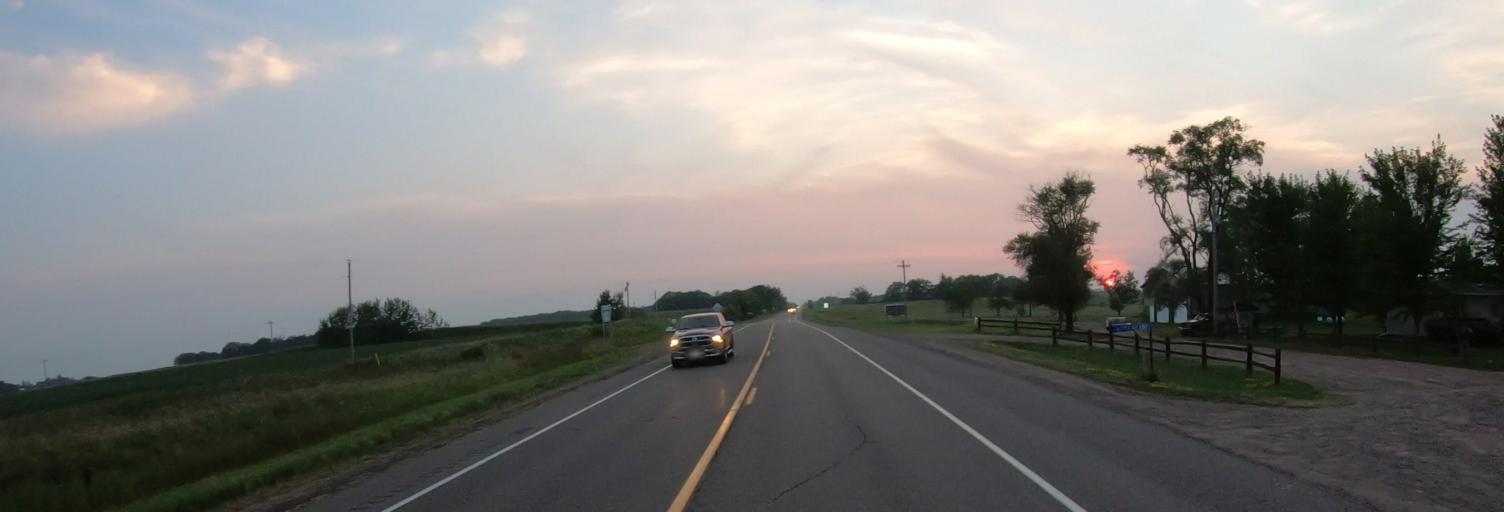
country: US
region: Minnesota
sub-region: Pine County
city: Rock Creek
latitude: 45.7666
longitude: -92.9686
